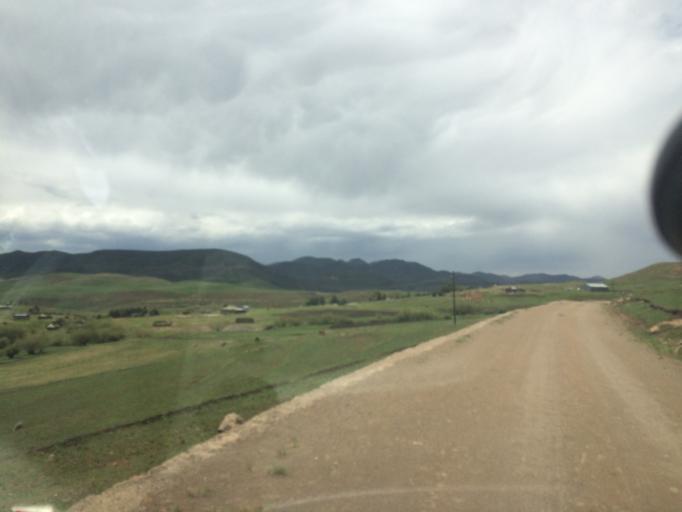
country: LS
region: Maseru
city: Nako
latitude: -29.8600
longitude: 28.0374
